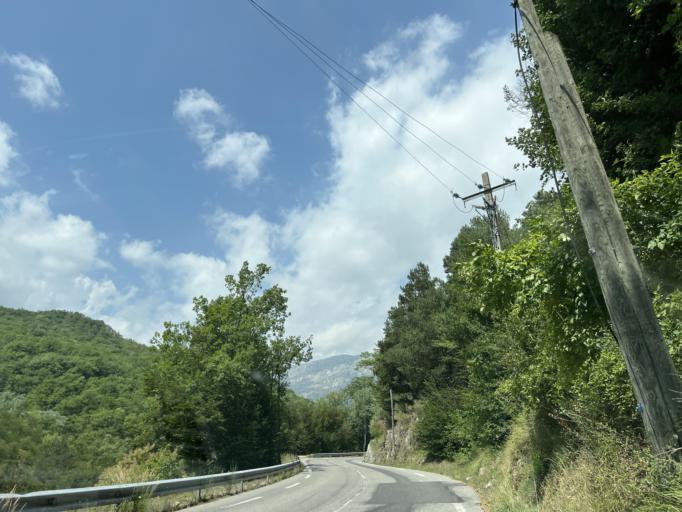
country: FR
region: Provence-Alpes-Cote d'Azur
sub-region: Departement des Alpes-Maritimes
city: Tourrettes-sur-Loup
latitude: 43.7684
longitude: 6.9854
